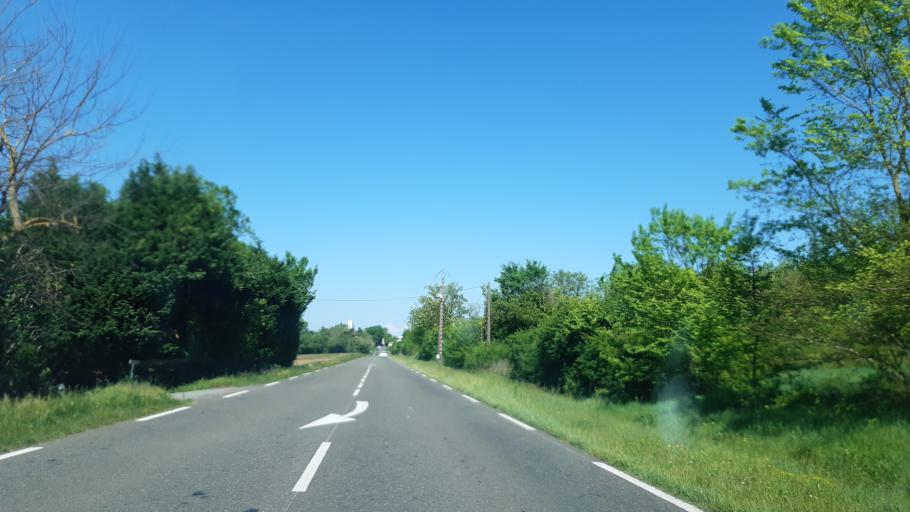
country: FR
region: Midi-Pyrenees
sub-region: Departement du Gers
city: Pujaudran
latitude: 43.5922
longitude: 1.0571
